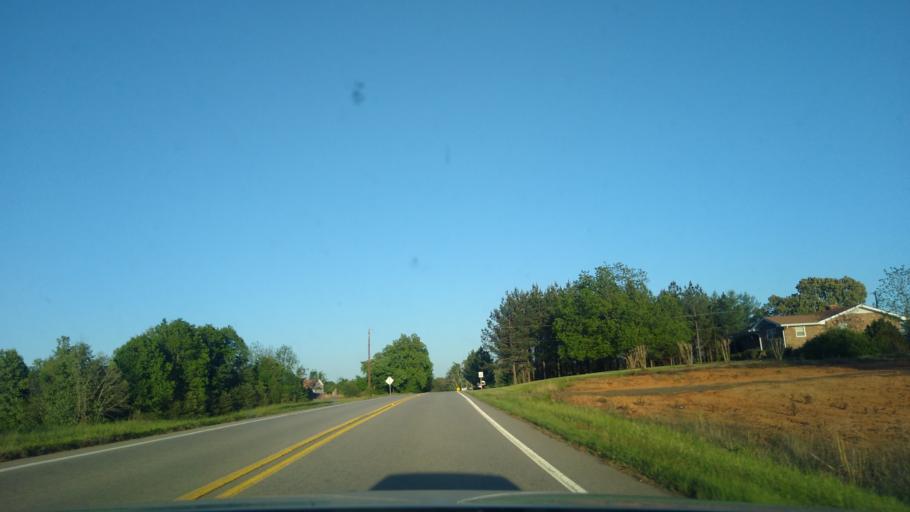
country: US
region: North Carolina
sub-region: Rockingham County
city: Reidsville
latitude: 36.3789
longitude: -79.5892
